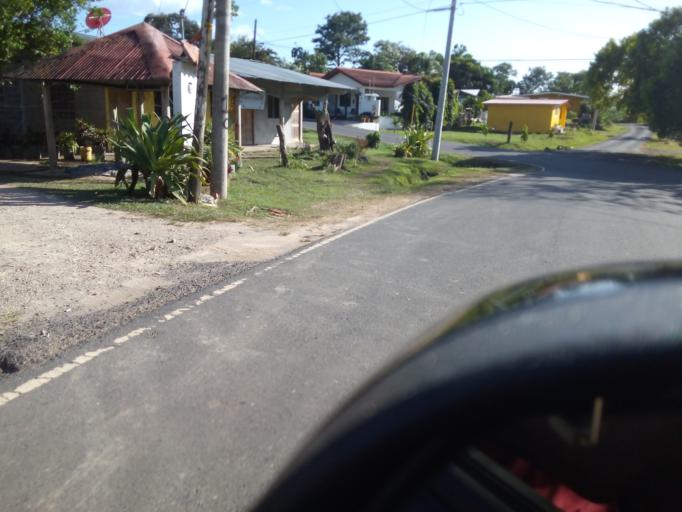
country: PA
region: Veraguas
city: Atalaya
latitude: 8.0434
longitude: -80.9267
